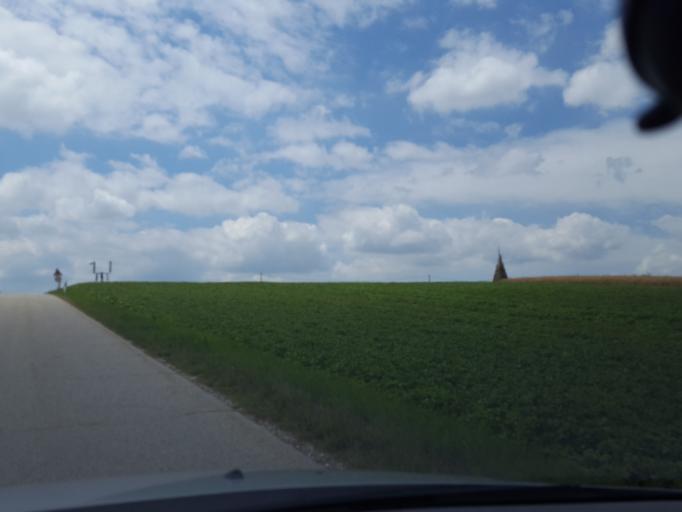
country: DE
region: Bavaria
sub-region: Upper Bavaria
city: Egglkofen
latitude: 48.3948
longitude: 12.4599
